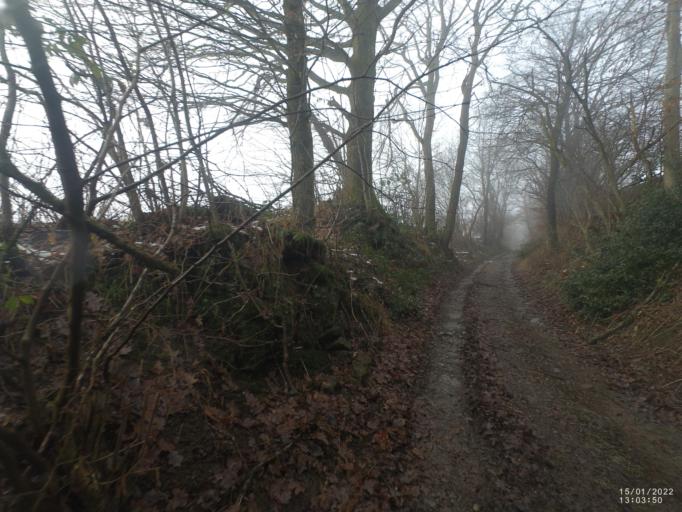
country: DE
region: North Rhine-Westphalia
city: Kierspe
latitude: 51.1117
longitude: 7.6028
